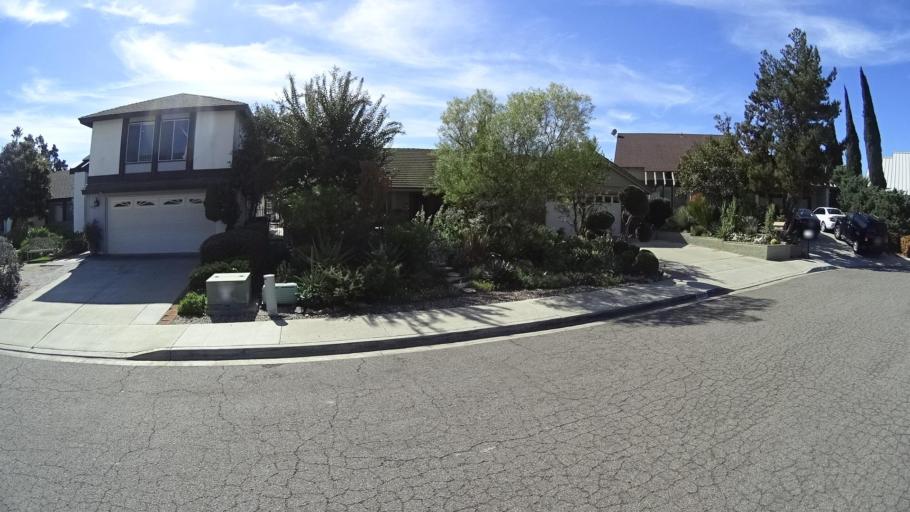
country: US
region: California
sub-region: San Diego County
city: Rancho San Diego
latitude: 32.7493
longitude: -116.9530
